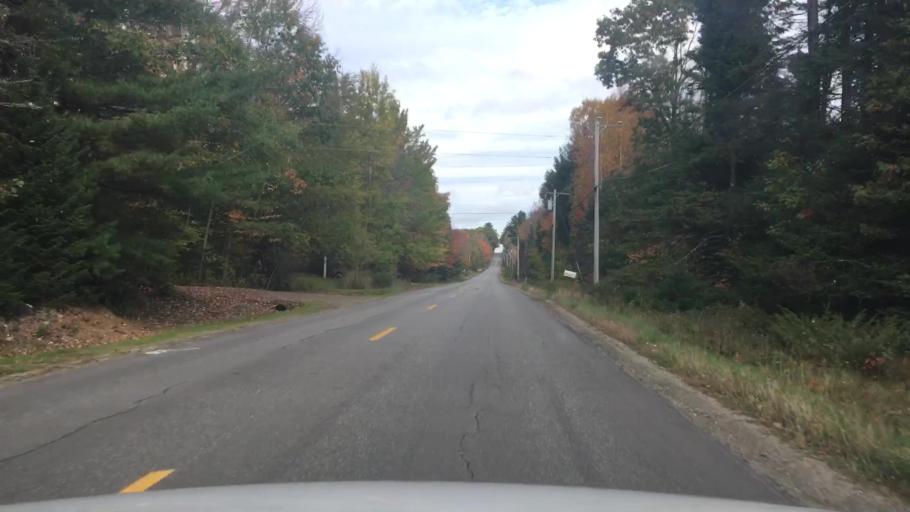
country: US
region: Maine
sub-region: Waldo County
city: Searsmont
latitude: 44.3843
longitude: -69.1323
